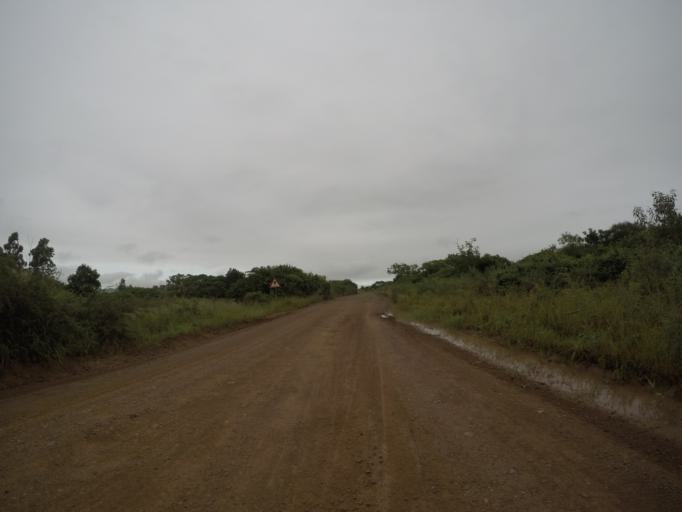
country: ZA
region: KwaZulu-Natal
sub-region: uThungulu District Municipality
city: Empangeni
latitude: -28.6579
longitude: 31.7865
